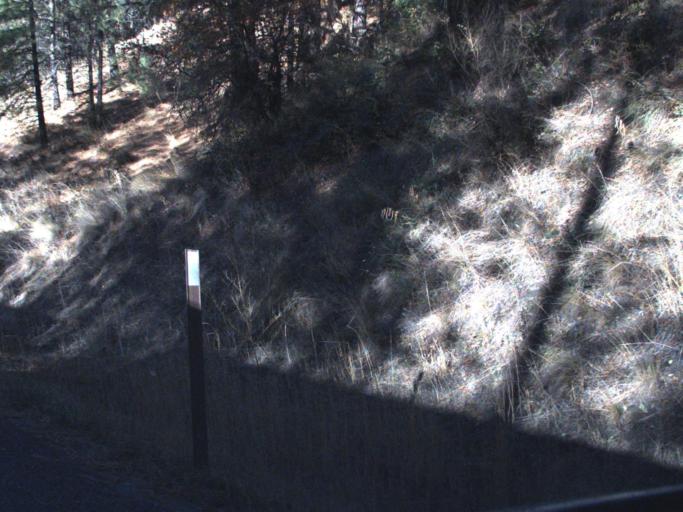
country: US
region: Washington
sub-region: Stevens County
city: Kettle Falls
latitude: 48.6143
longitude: -118.0782
